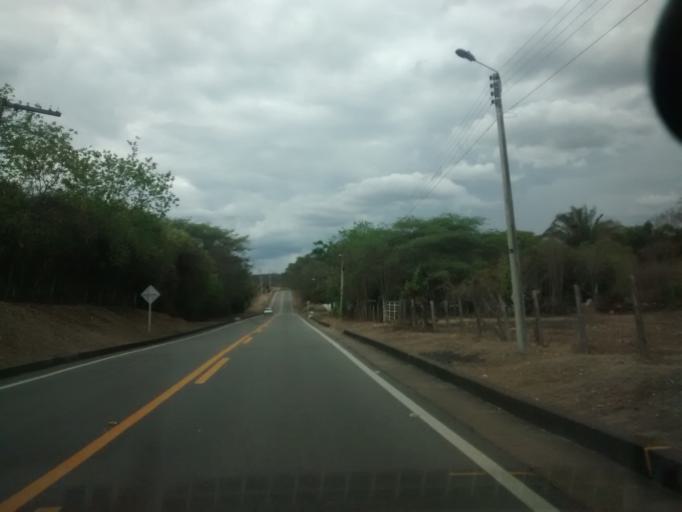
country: CO
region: Cundinamarca
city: Agua de Dios
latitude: 4.4221
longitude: -74.7033
